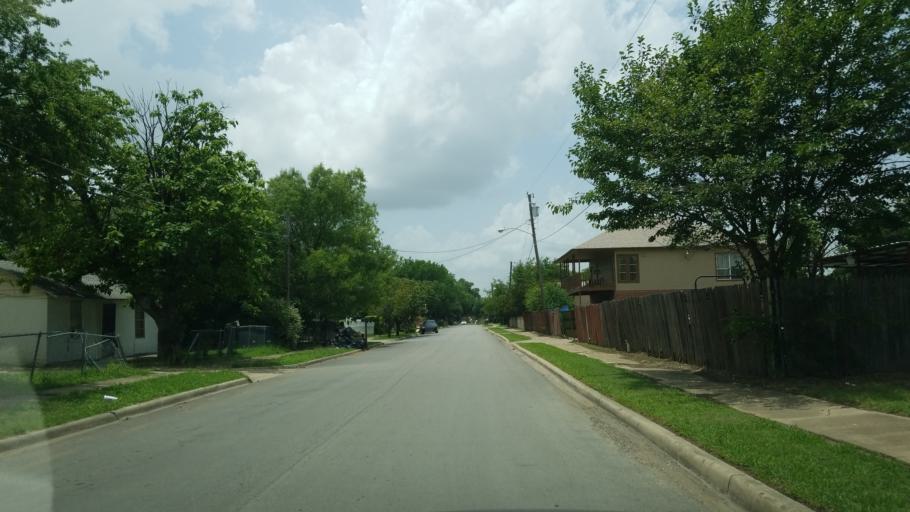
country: US
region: Texas
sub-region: Dallas County
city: Cockrell Hill
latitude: 32.7828
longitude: -96.9036
